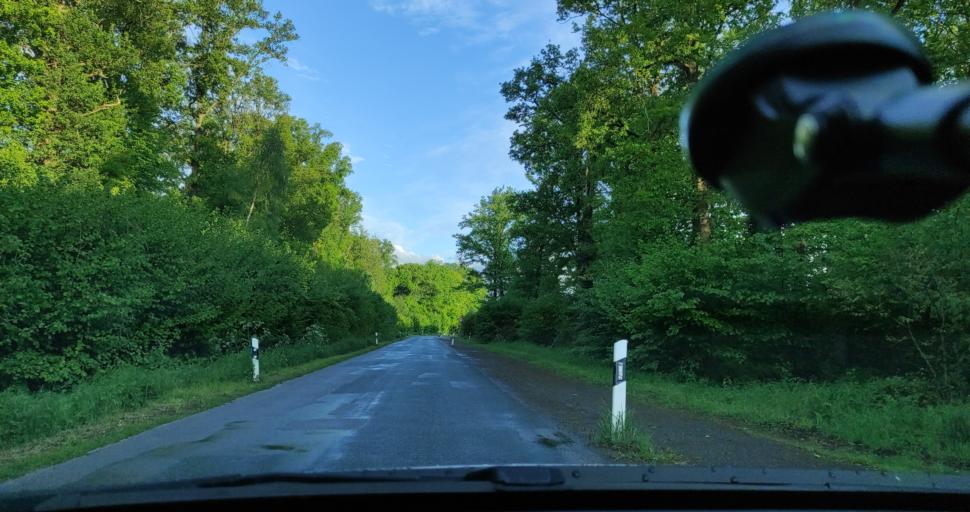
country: DE
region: North Rhine-Westphalia
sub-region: Regierungsbezirk Munster
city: Greven
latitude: 52.0801
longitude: 7.5740
